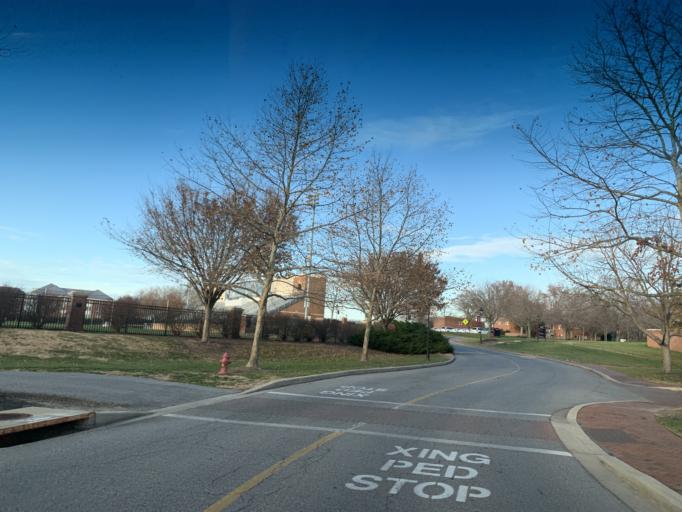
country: US
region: Maryland
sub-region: Kent County
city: Chestertown
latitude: 39.2177
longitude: -76.0703
